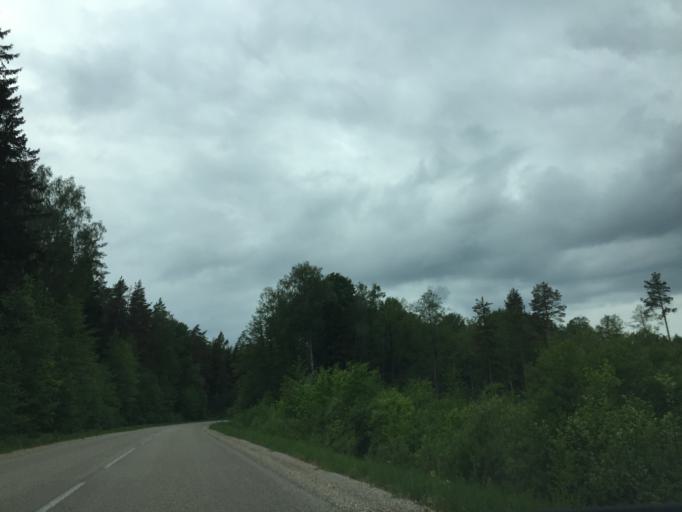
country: LV
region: Varkava
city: Vecvarkava
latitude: 56.0748
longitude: 26.6314
